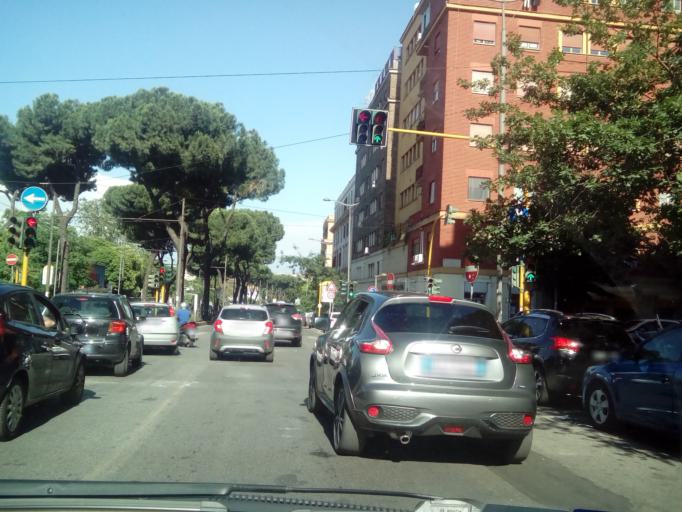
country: IT
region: Latium
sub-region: Citta metropolitana di Roma Capitale
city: Rome
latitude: 41.8922
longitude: 12.5338
